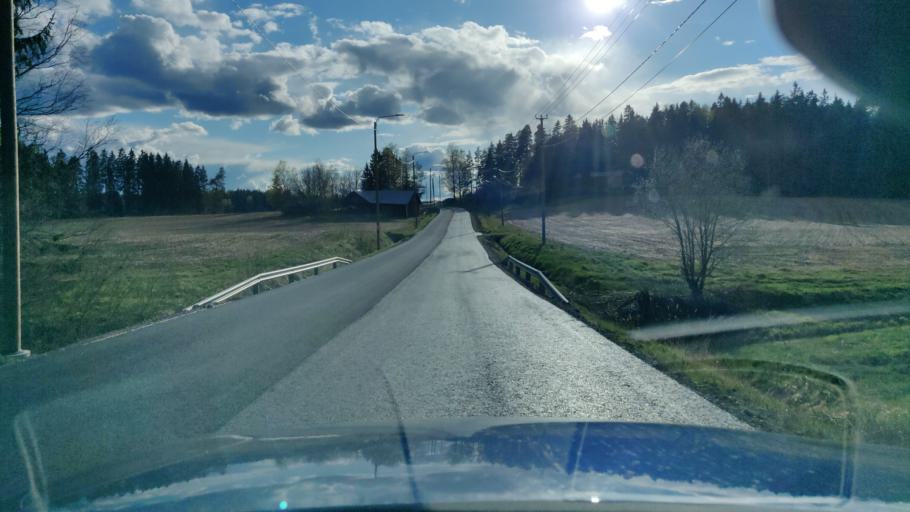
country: FI
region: Uusimaa
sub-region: Helsinki
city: Nurmijaervi
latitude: 60.3588
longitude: 24.7084
